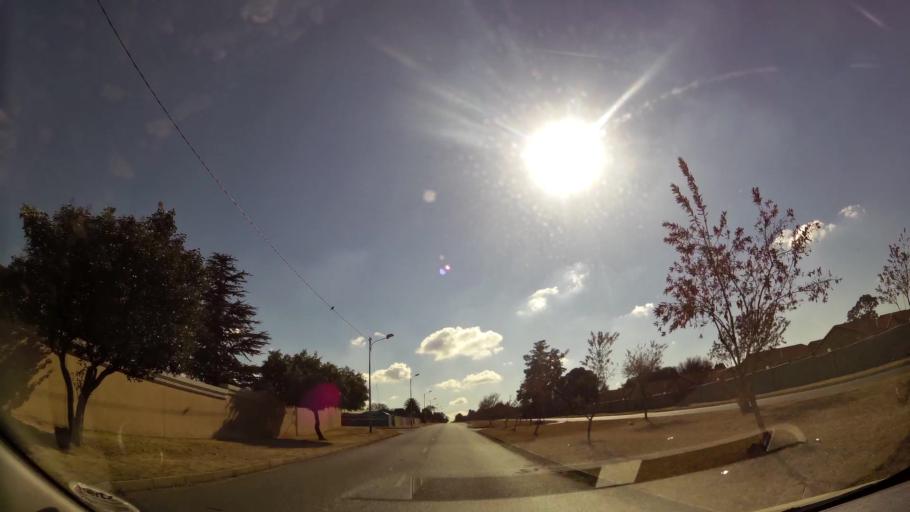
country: ZA
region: Gauteng
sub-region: City of Johannesburg Metropolitan Municipality
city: Roodepoort
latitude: -26.1463
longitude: 27.8341
